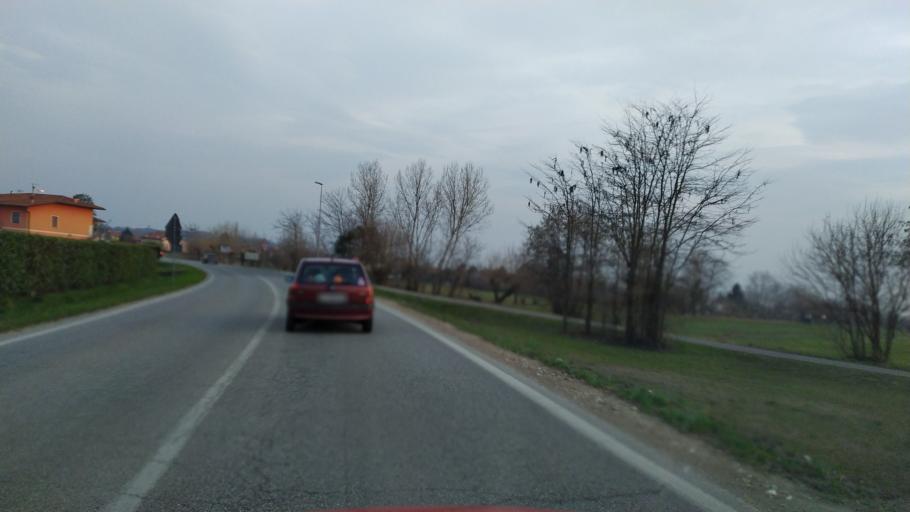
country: IT
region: Veneto
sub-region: Provincia di Vicenza
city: Preara-Moraro-Leva Nord
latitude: 45.6839
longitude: 11.5339
